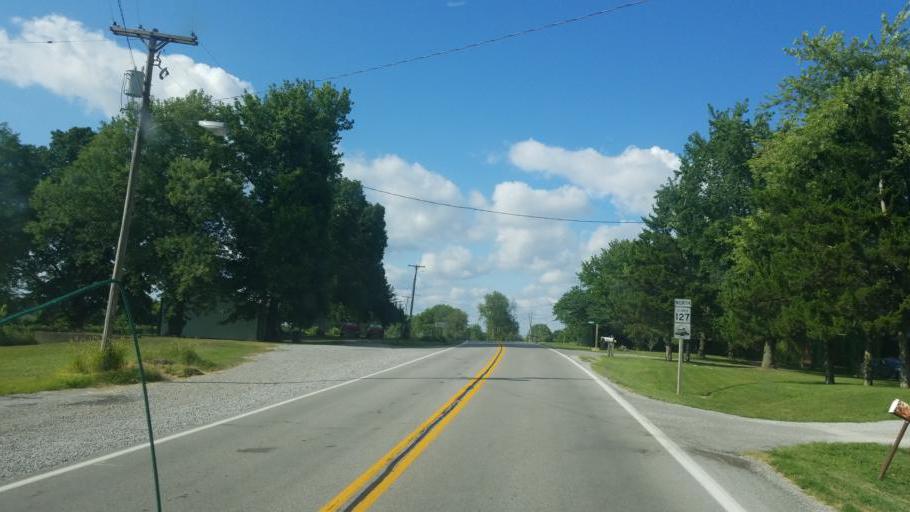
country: US
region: Illinois
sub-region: Union County
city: Cobden
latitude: 37.5767
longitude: -89.3208
